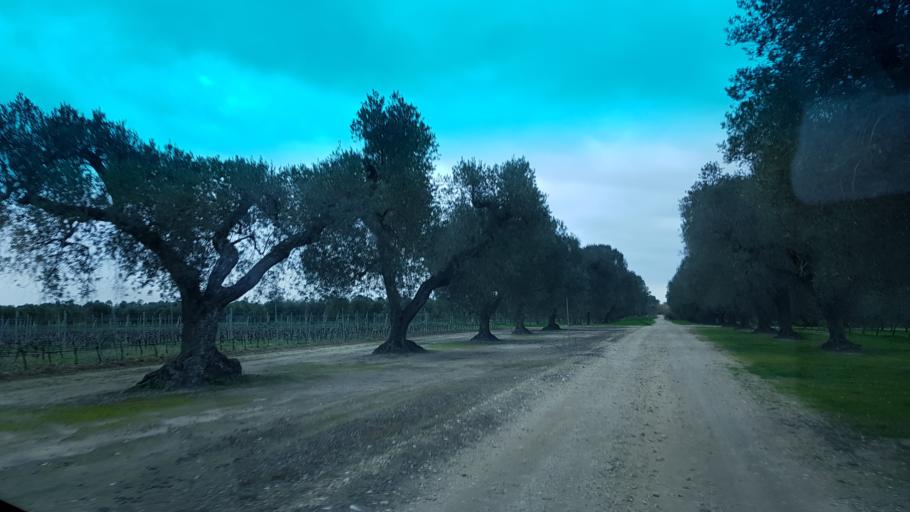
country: IT
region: Apulia
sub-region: Provincia di Brindisi
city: La Rosa
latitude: 40.5854
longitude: 17.9873
